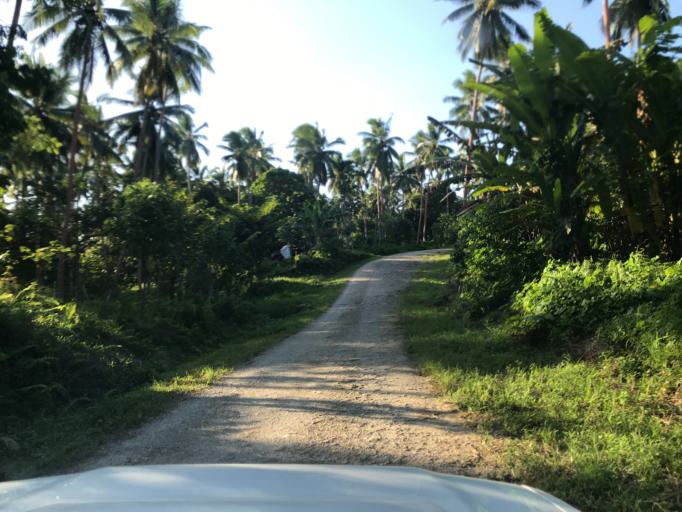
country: VU
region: Sanma
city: Luganville
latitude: -15.5925
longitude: 166.8984
